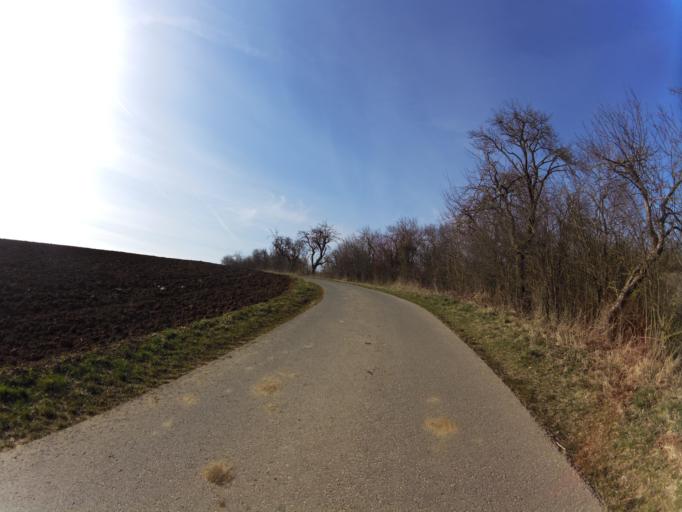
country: DE
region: Bavaria
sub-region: Regierungsbezirk Unterfranken
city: Prosselsheim
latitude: 49.8297
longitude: 10.1171
